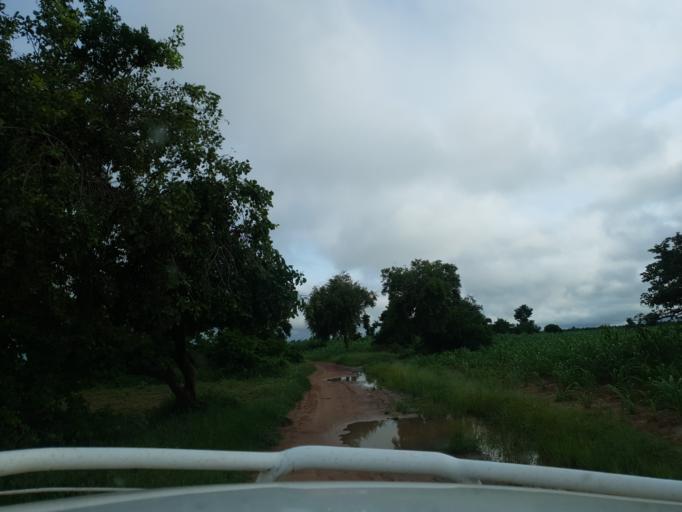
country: ML
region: Segou
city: Baroueli
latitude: 13.4019
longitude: -7.0066
